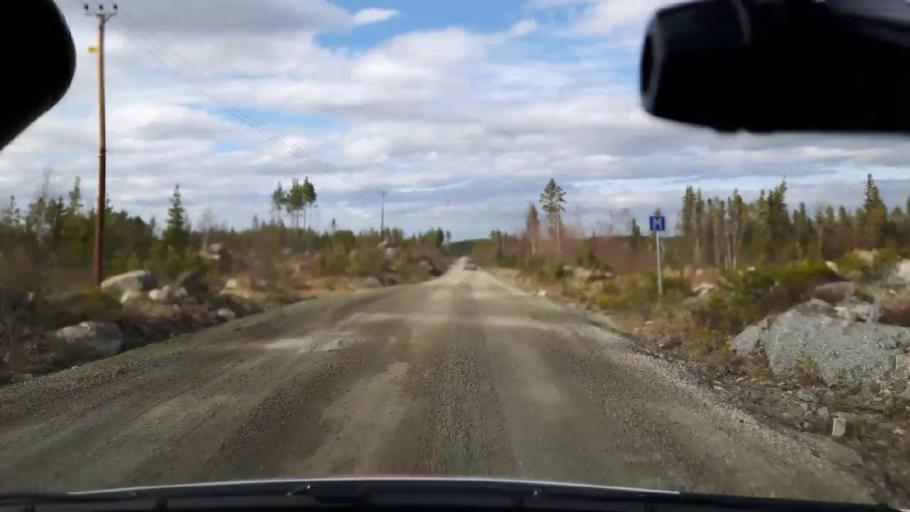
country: SE
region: Jaemtland
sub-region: Bergs Kommun
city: Hoverberg
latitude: 62.8405
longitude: 14.6668
